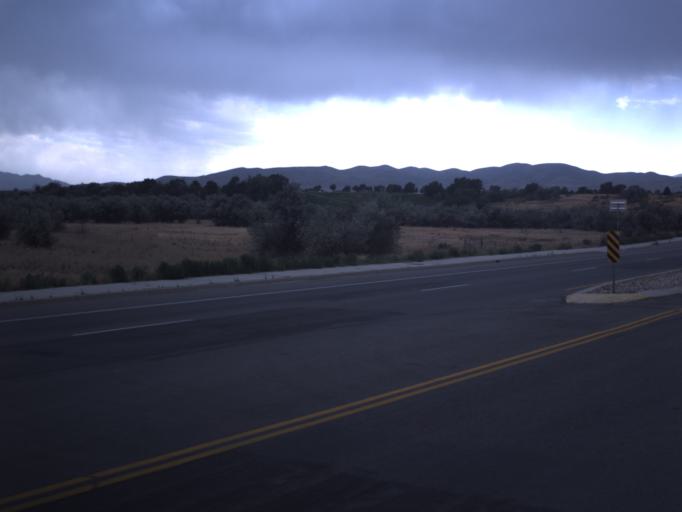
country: US
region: Utah
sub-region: Salt Lake County
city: Riverton
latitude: 40.5261
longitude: -111.9173
